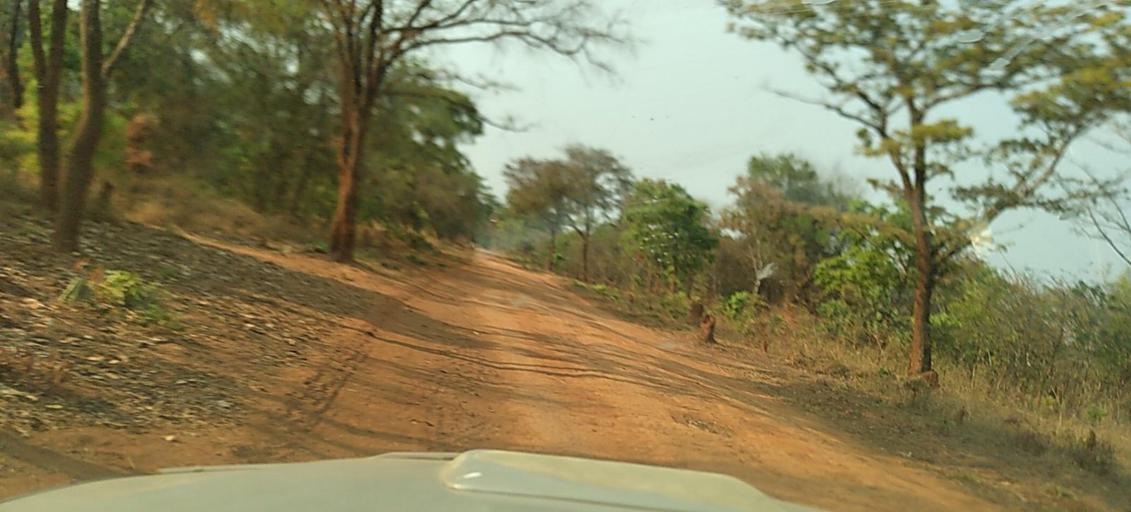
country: ZM
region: North-Western
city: Kasempa
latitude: -13.2929
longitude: 26.5548
